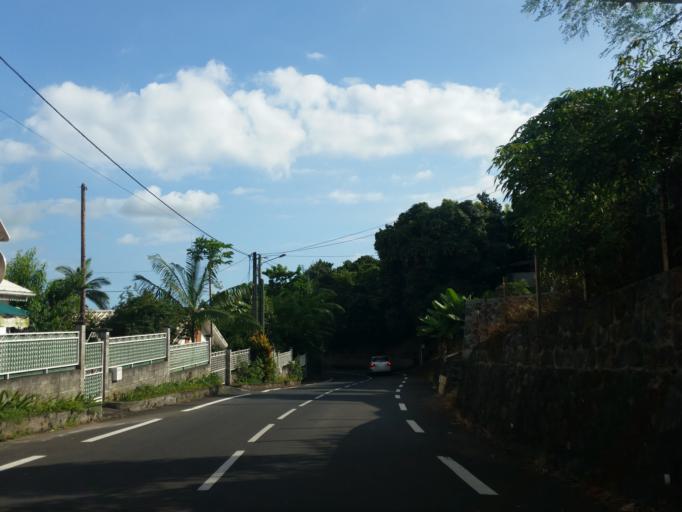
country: RE
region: Reunion
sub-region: Reunion
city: L'Entre-Deux
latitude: -21.2422
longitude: 55.4806
